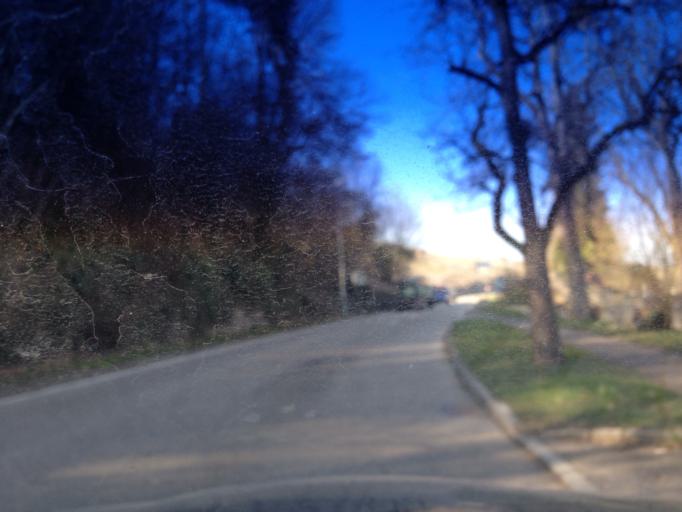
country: DE
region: Baden-Wuerttemberg
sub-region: Karlsruhe Region
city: Illingen
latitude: 48.9411
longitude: 8.8897
